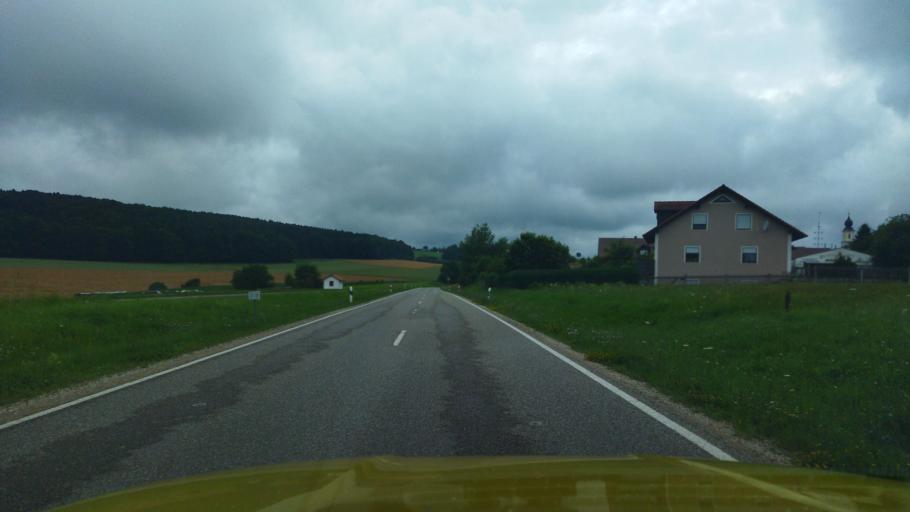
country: DE
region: Bavaria
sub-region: Upper Palatinate
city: Dietfurt
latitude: 48.9480
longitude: 11.5924
